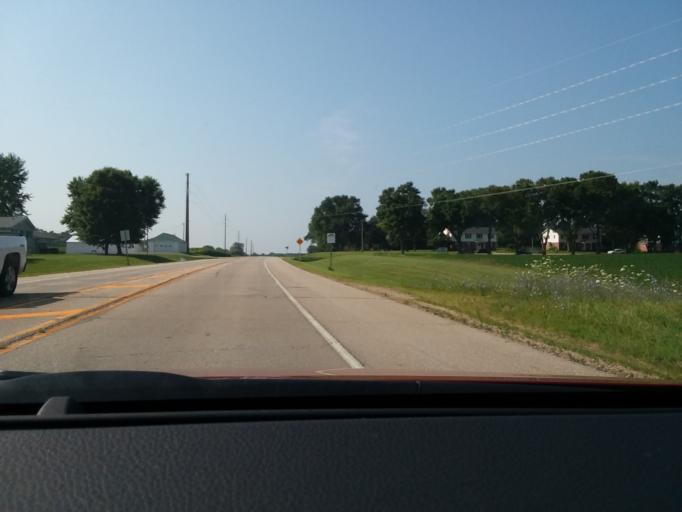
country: US
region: Wisconsin
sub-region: Dane County
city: Waunakee
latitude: 43.1849
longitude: -89.4117
